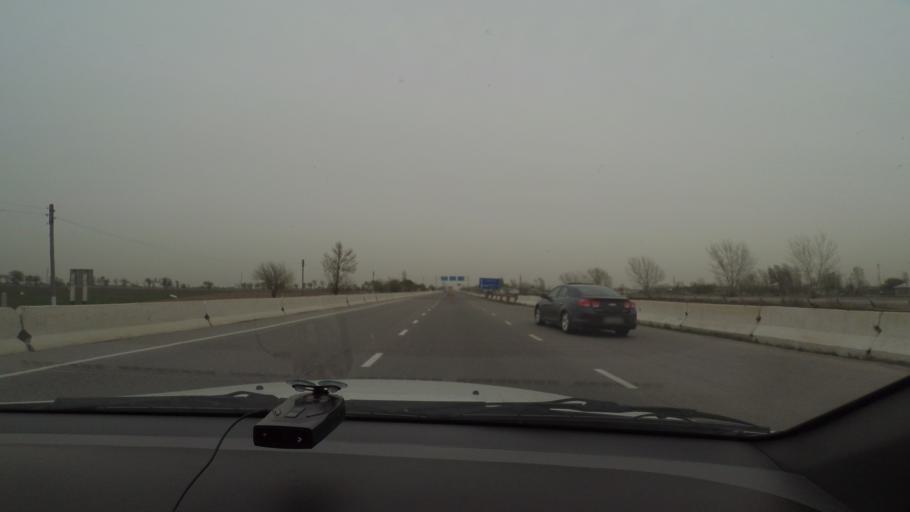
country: UZ
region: Jizzax
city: Gagarin
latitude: 40.4922
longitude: 68.2990
